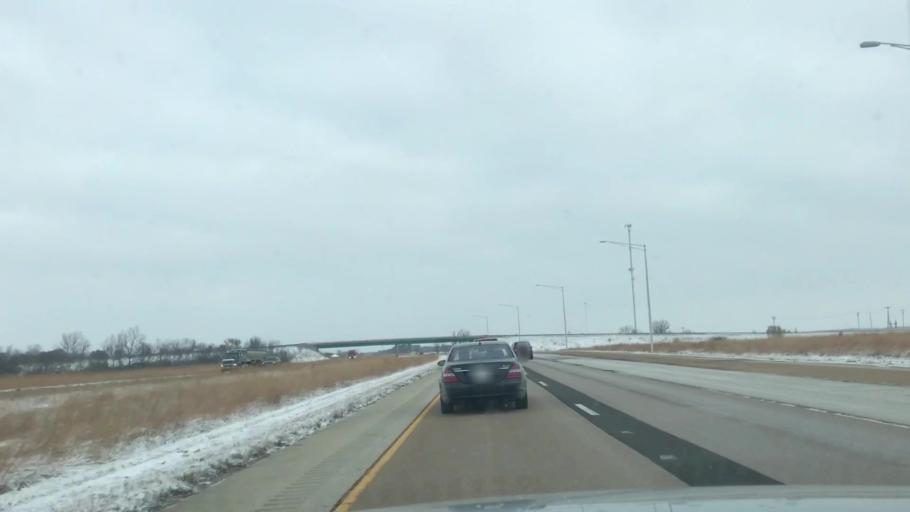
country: US
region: Illinois
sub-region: Montgomery County
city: Litchfield
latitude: 39.2308
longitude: -89.6426
